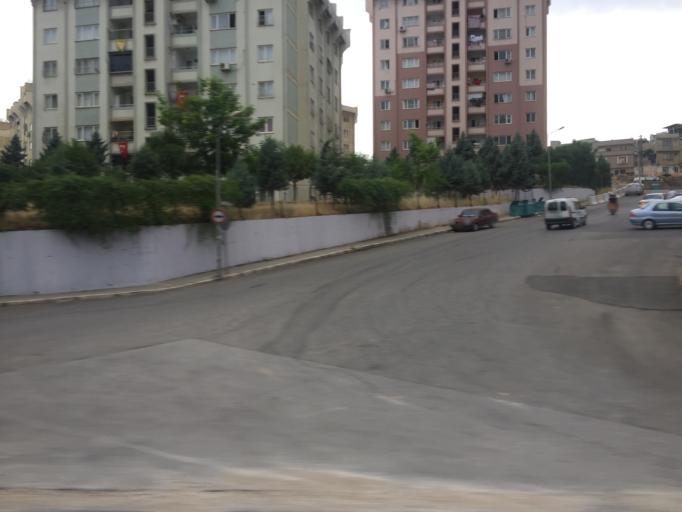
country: TR
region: Gaziantep
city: Gaziantep
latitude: 37.0505
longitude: 37.4214
